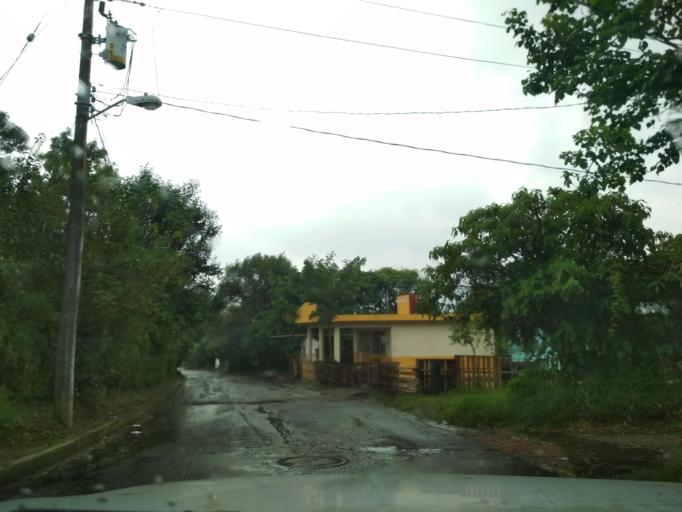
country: MX
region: Veracruz
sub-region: Ixhuatlancillo
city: San Isidro
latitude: 18.8999
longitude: -97.1210
